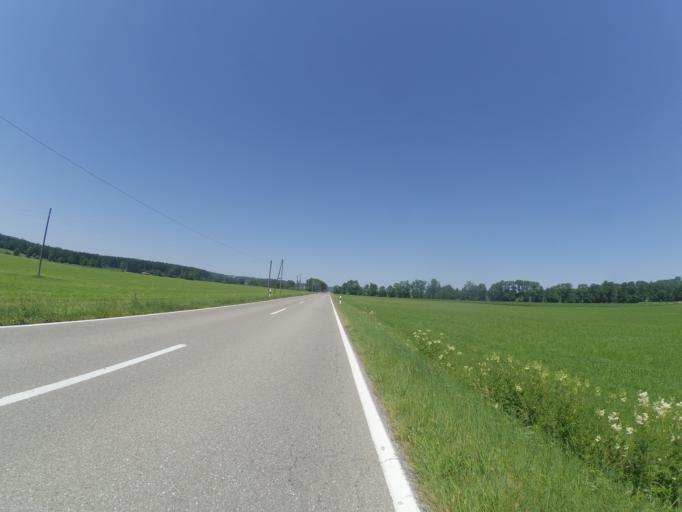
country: DE
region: Bavaria
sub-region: Swabia
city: Bohen
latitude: 47.8936
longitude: 10.3232
